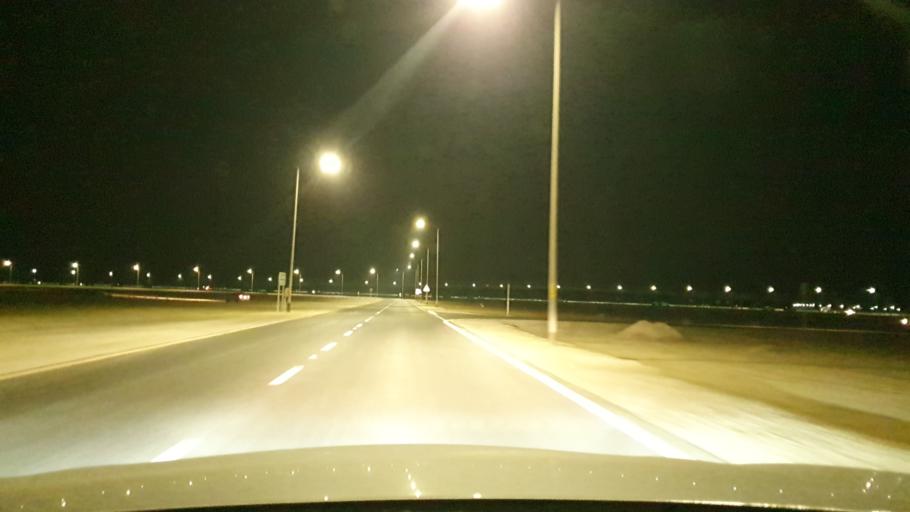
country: BH
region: Muharraq
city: Al Muharraq
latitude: 26.2845
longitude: 50.5817
